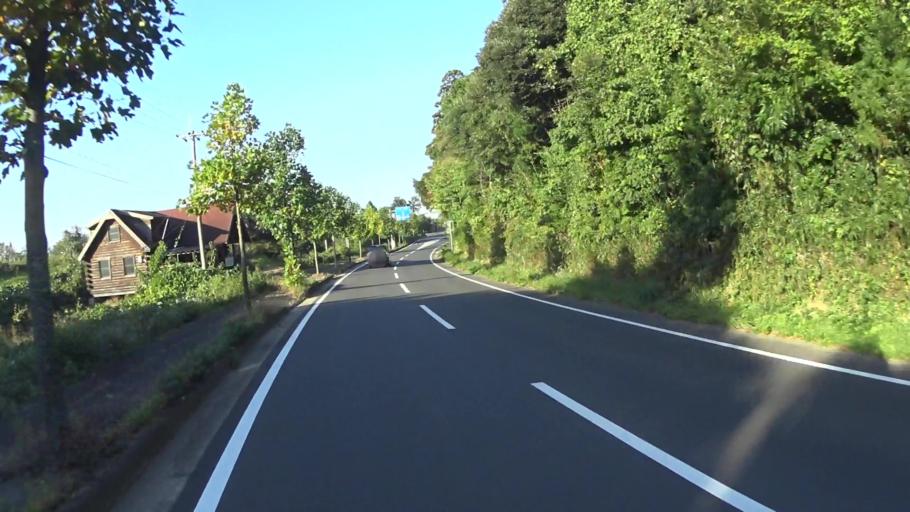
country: JP
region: Hyogo
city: Toyooka
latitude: 35.6250
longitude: 134.9284
